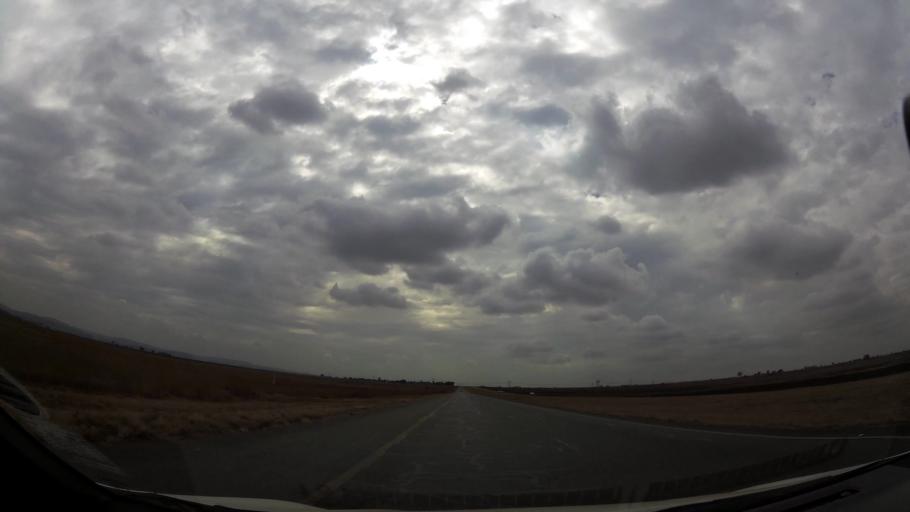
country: ZA
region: Gauteng
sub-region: Ekurhuleni Metropolitan Municipality
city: Germiston
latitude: -26.3720
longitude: 28.0914
